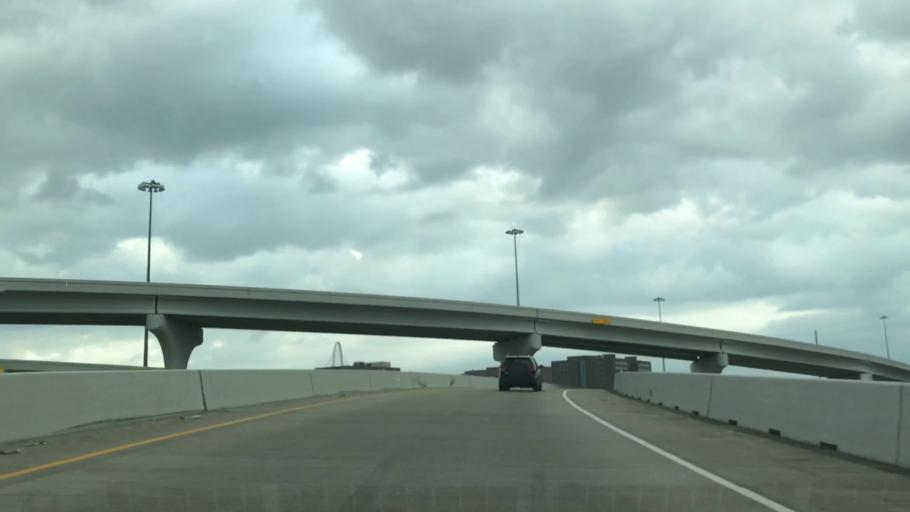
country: US
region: Texas
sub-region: Dallas County
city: Dallas
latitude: 32.7717
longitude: -96.8097
